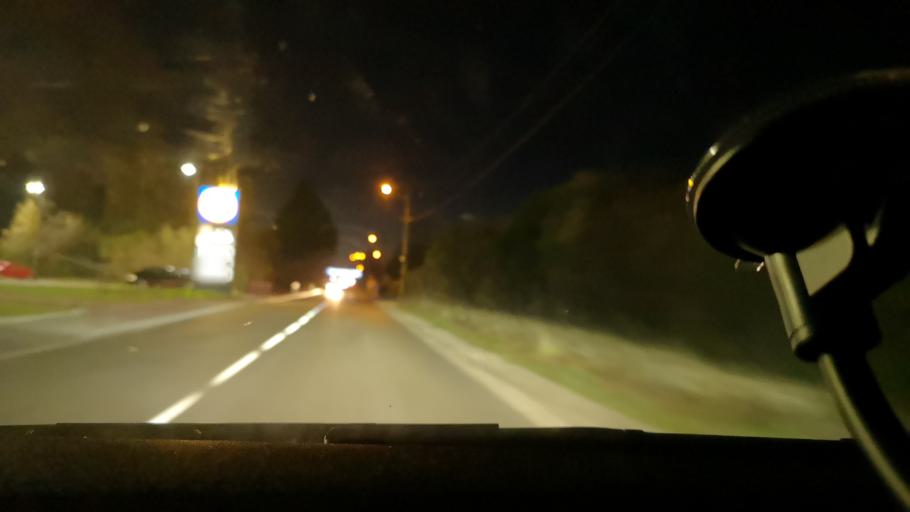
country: FR
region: Franche-Comte
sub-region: Departement du Jura
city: Bletterans
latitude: 46.7486
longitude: 5.4654
